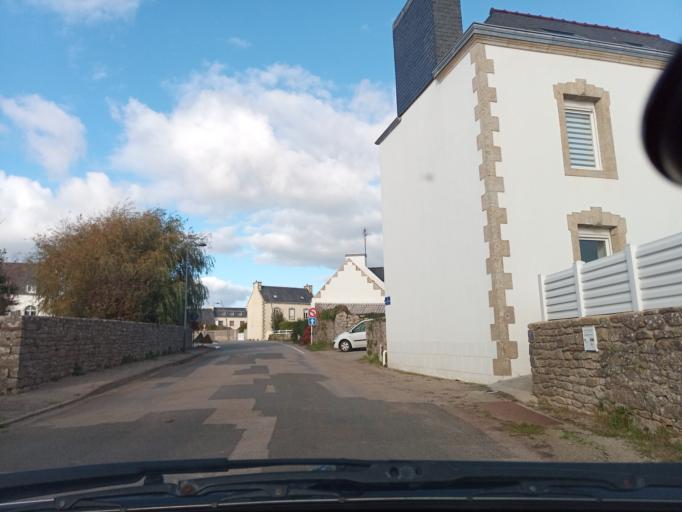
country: FR
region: Brittany
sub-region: Departement du Finistere
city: Plouhinec
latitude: 48.0131
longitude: -4.4889
